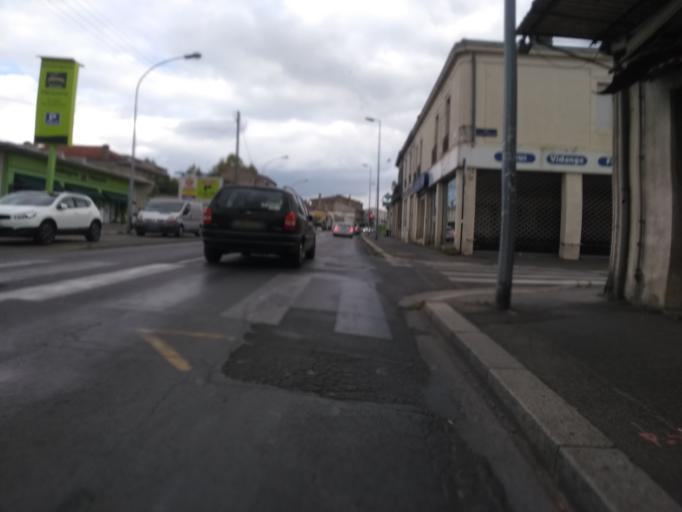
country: FR
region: Aquitaine
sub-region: Departement de la Gironde
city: Talence
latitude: 44.8118
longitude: -0.5737
